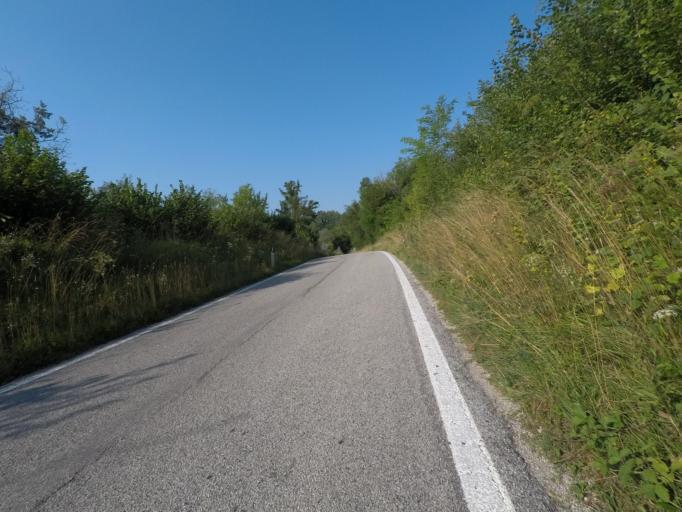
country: IT
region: Friuli Venezia Giulia
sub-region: Provincia di Udine
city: Forgaria nel Friuli
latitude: 46.2093
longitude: 12.9741
